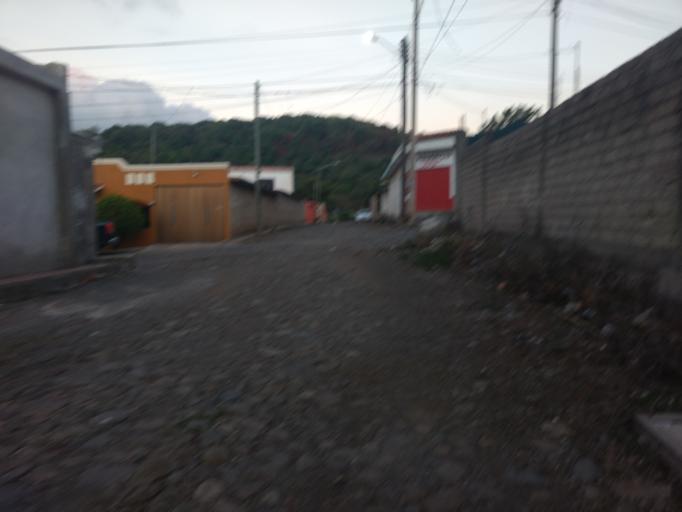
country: MX
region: Nayarit
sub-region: Tepic
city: La Corregidora
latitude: 21.4607
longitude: -104.8003
